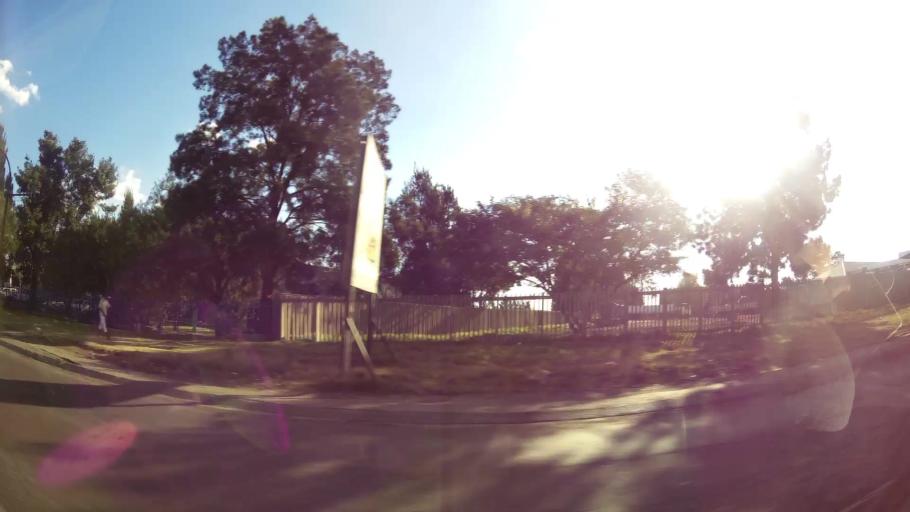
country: ZA
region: Mpumalanga
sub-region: Nkangala District Municipality
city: Witbank
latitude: -25.8700
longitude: 29.1661
